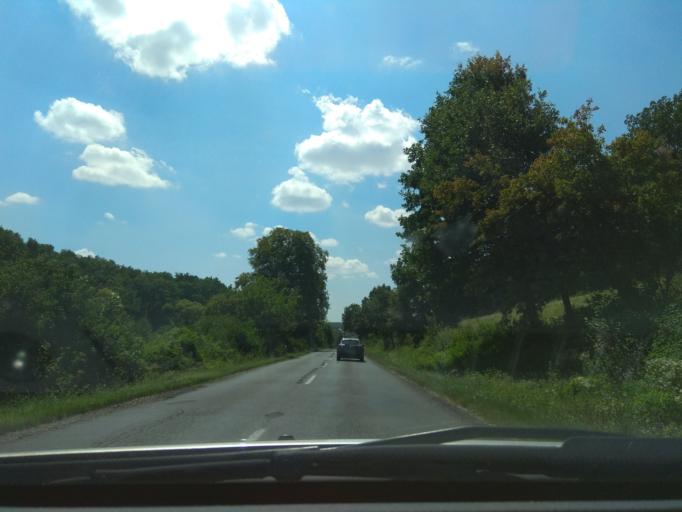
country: HU
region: Borsod-Abauj-Zemplen
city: Harsany
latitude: 48.0082
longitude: 20.7625
